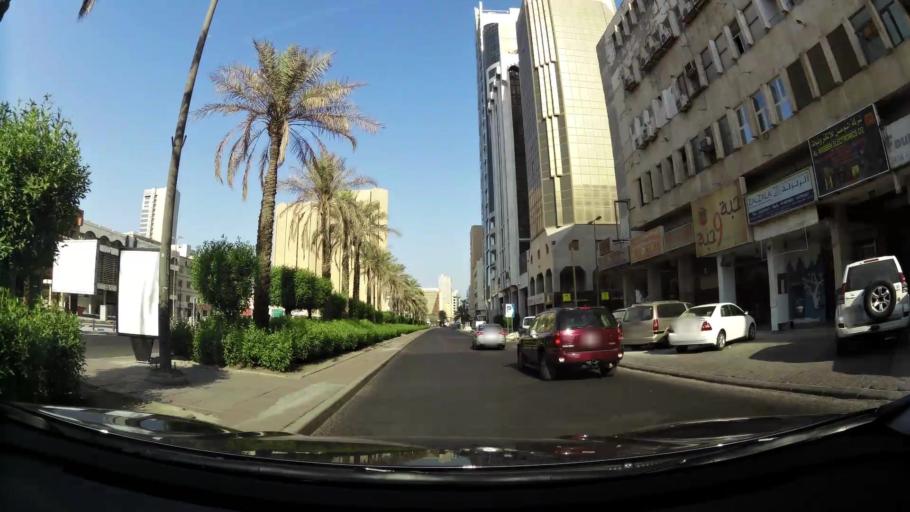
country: KW
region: Al Asimah
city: Kuwait City
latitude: 29.3734
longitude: 47.9806
